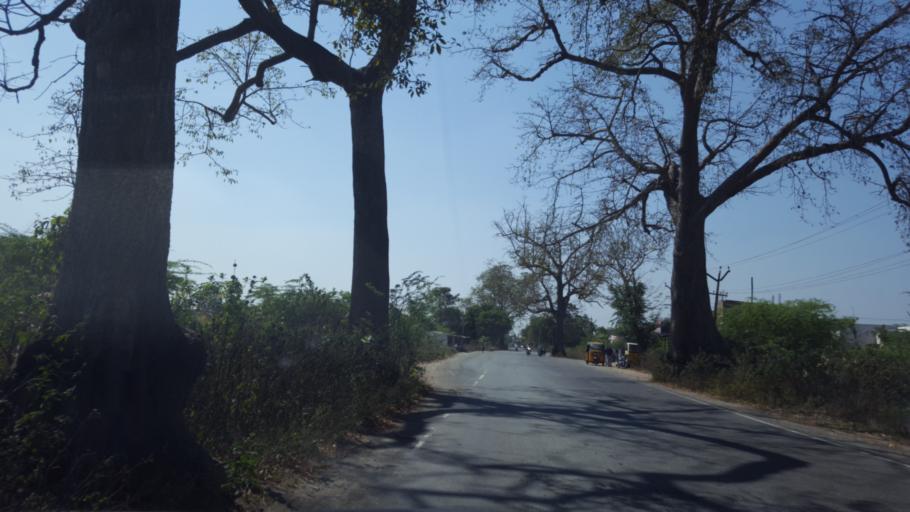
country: IN
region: Tamil Nadu
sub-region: Kancheepuram
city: Wallajahbad
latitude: 12.7846
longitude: 79.8376
